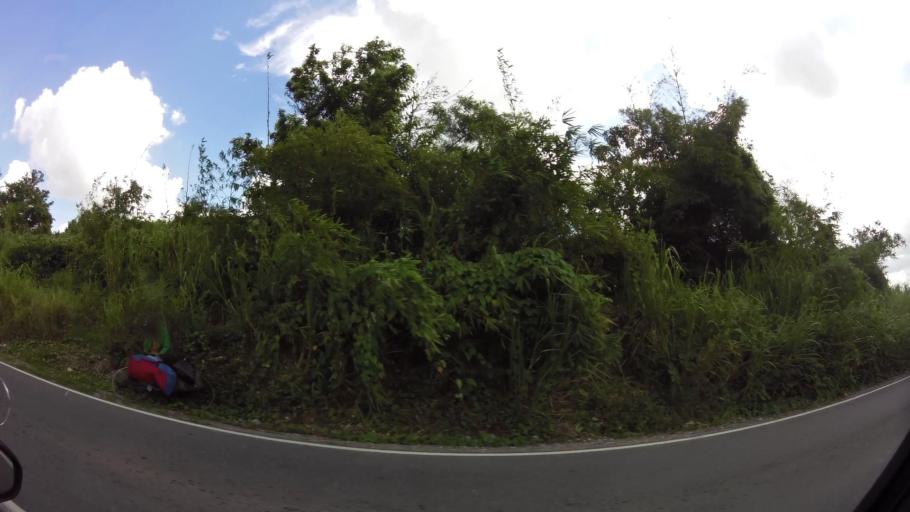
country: TT
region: Penal/Debe
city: Debe
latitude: 10.2308
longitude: -61.4847
